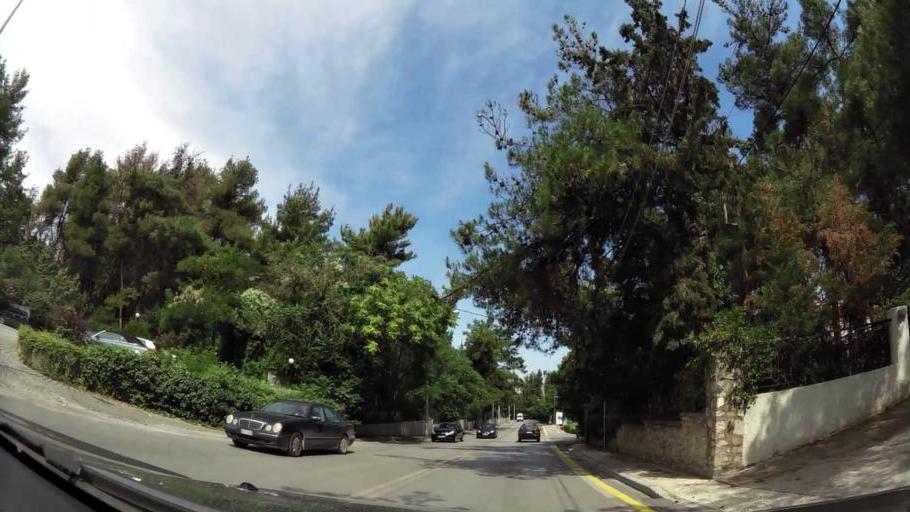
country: GR
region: Central Macedonia
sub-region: Nomos Thessalonikis
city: Pylaia
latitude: 40.5945
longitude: 23.0071
